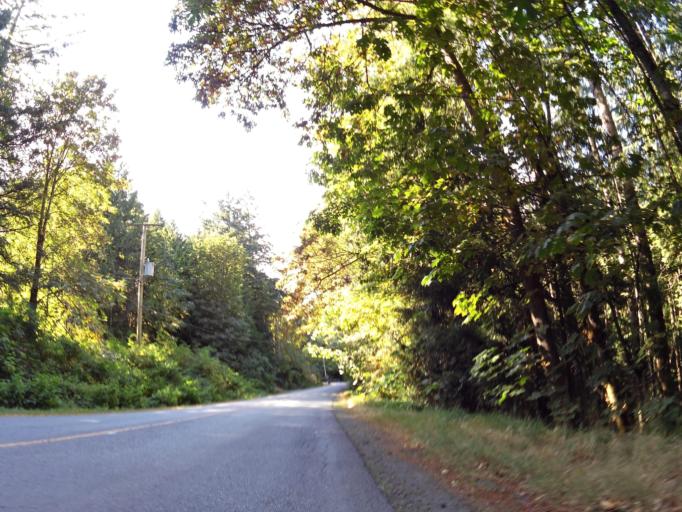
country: CA
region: British Columbia
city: North Saanich
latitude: 48.6932
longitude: -123.5638
